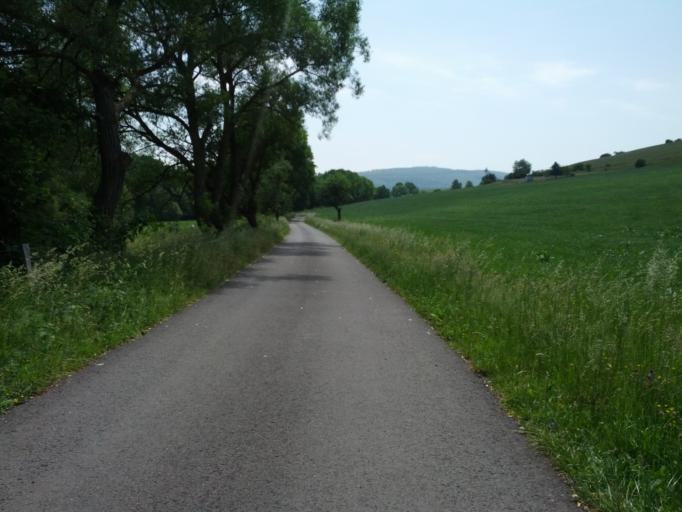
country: DE
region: Thuringia
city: Wiesenthal
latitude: 50.7170
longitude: 10.1637
